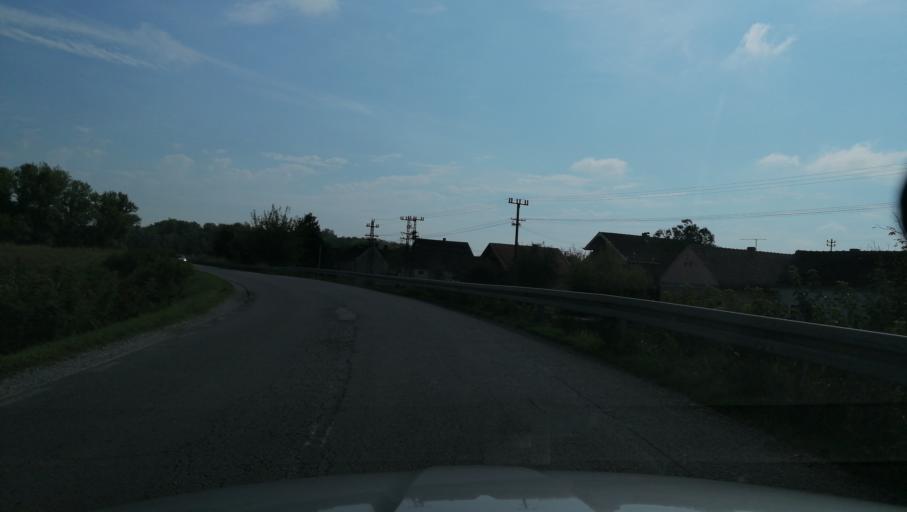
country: RS
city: Bosut
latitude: 44.9413
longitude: 19.3660
